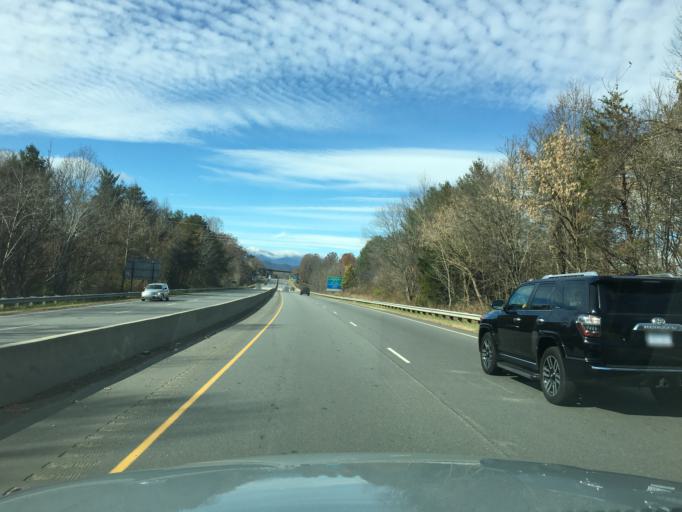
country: US
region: North Carolina
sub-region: McDowell County
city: Marion
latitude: 35.6737
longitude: -82.0156
